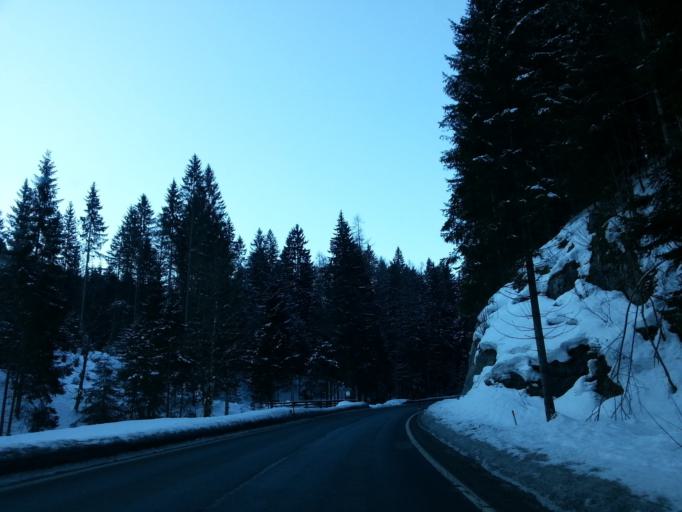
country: AT
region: Salzburg
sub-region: Politischer Bezirk Sankt Johann im Pongau
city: Eben im Pongau
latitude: 47.4765
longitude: 13.3913
